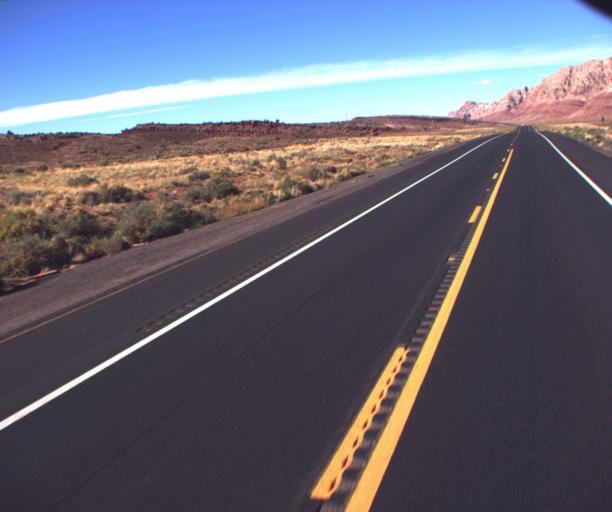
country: US
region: Arizona
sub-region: Coconino County
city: LeChee
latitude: 36.4814
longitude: -111.5742
